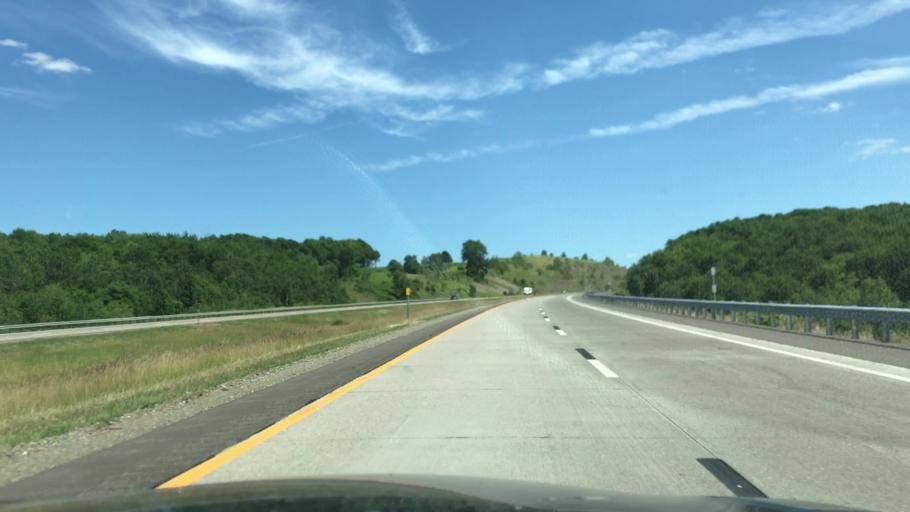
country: US
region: New York
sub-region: Steuben County
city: Wayland
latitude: 42.5366
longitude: -77.5630
